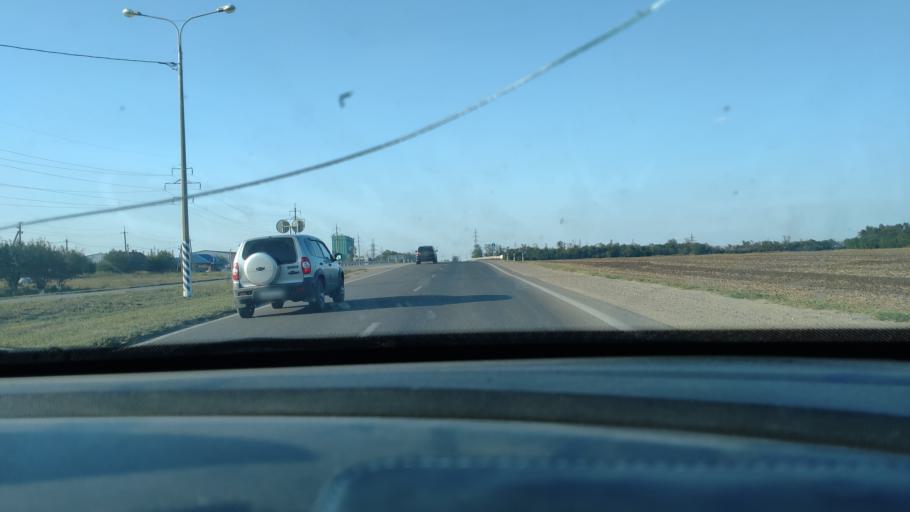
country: RU
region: Krasnodarskiy
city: Timashevsk
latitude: 45.6106
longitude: 38.9877
